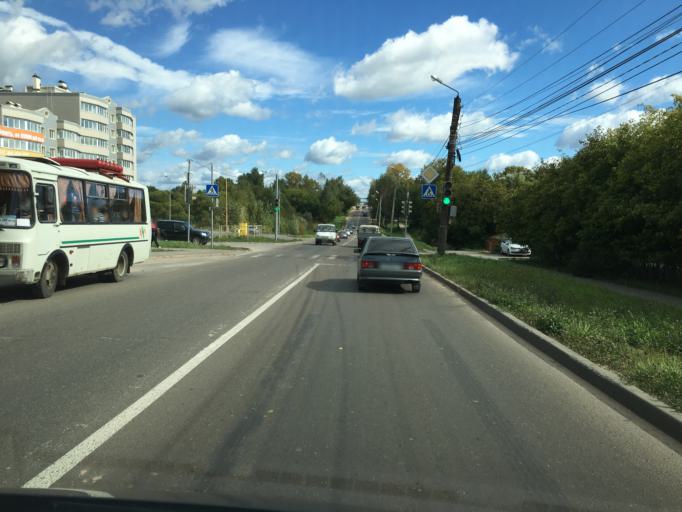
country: RU
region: Kaluga
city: Kaluga
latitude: 54.5437
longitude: 36.3240
